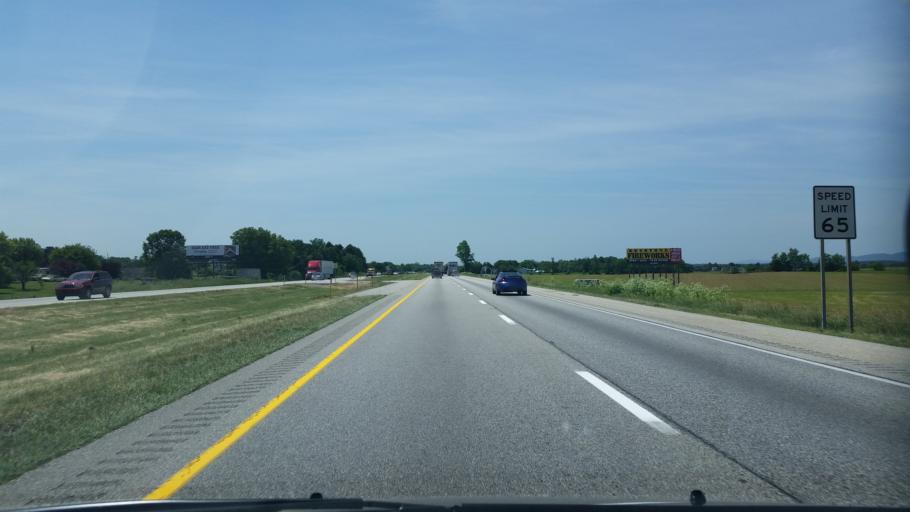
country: US
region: Pennsylvania
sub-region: Franklin County
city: Greencastle
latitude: 39.8448
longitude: -77.6911
